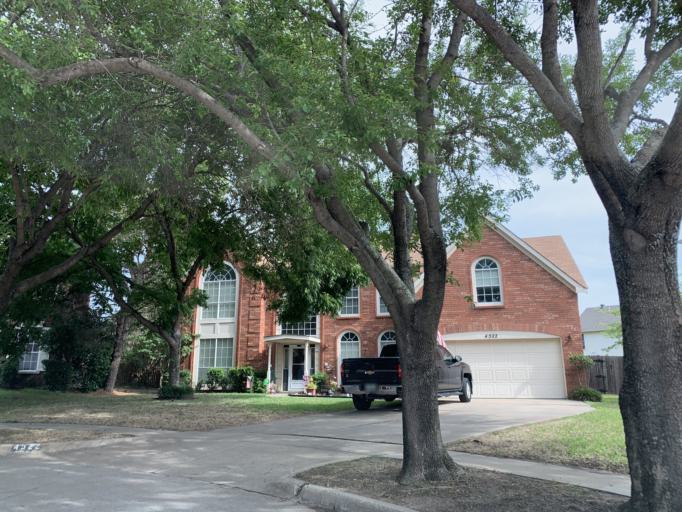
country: US
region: Texas
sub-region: Dallas County
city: Grand Prairie
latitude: 32.6616
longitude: -97.0112
